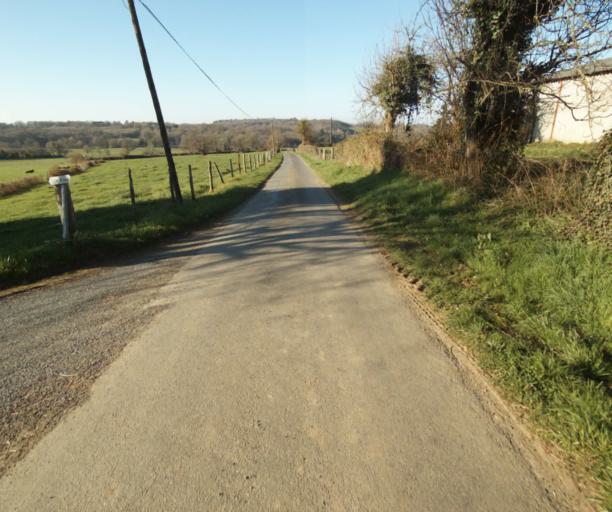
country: FR
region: Limousin
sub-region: Departement de la Correze
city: Uzerche
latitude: 45.3836
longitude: 1.5872
